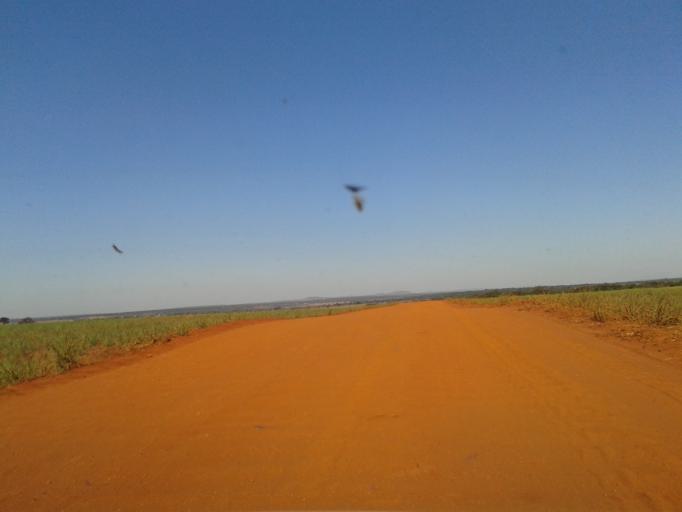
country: BR
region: Minas Gerais
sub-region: Santa Vitoria
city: Santa Vitoria
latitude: -18.8432
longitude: -50.0578
